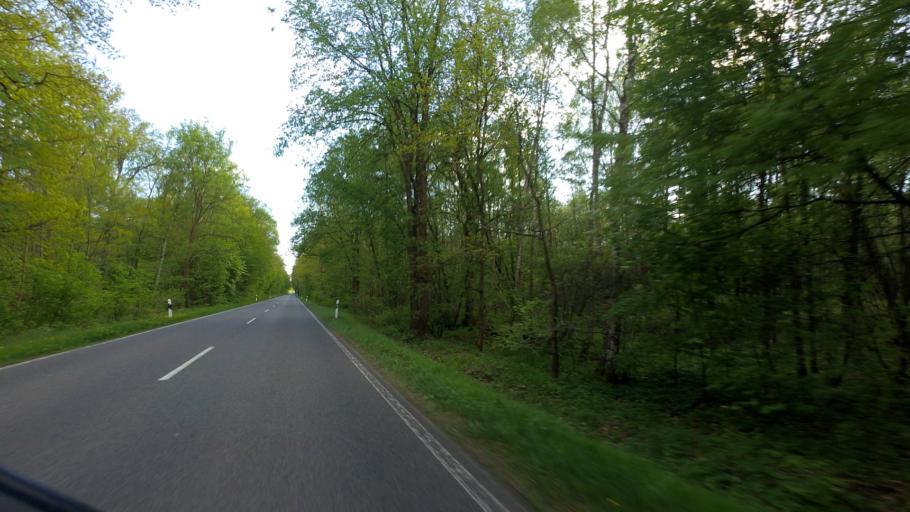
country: DE
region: Brandenburg
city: Liebenwalde
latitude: 52.8120
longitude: 13.4064
